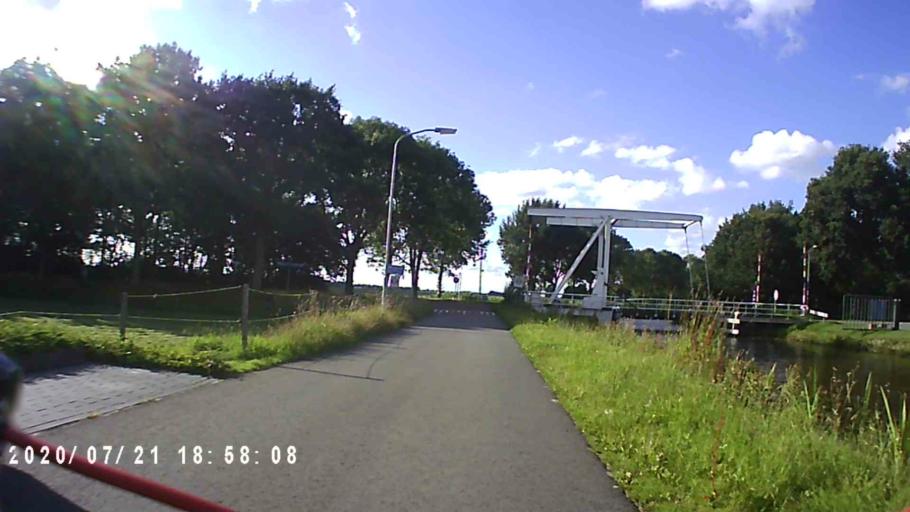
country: NL
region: Groningen
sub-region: Gemeente Hoogezand-Sappemeer
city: Hoogezand
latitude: 53.2175
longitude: 6.7387
